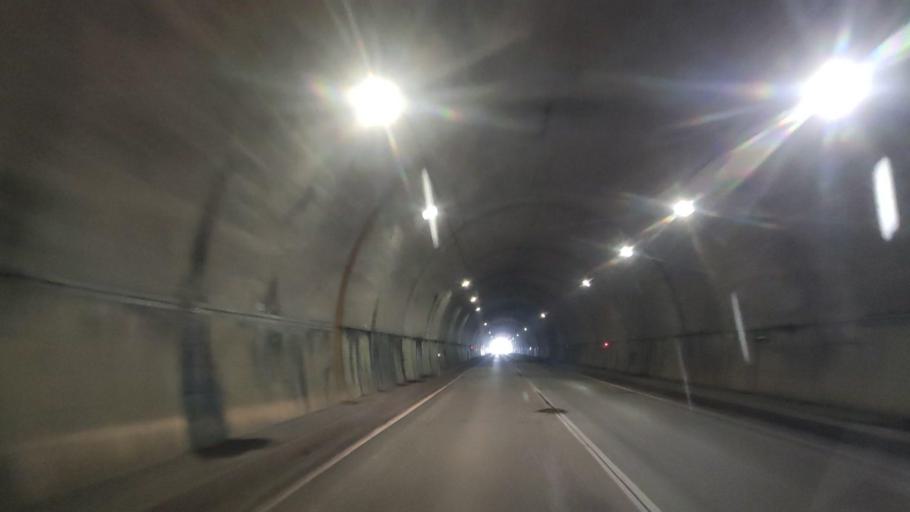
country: JP
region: Nagano
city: Iiyama
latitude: 36.8670
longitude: 138.3642
